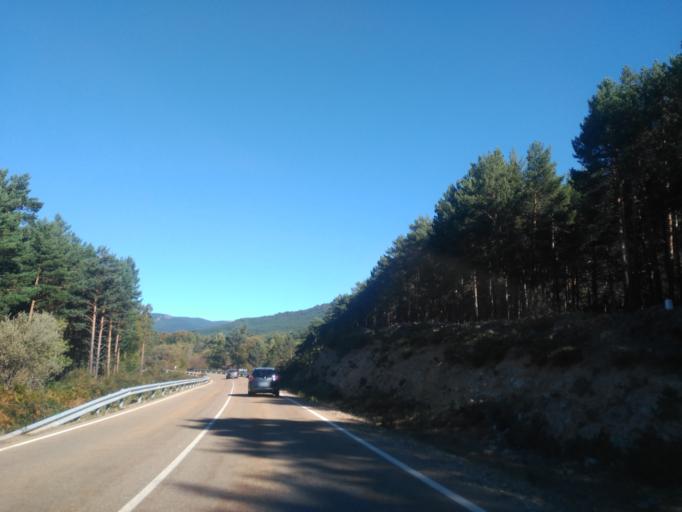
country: ES
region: Castille and Leon
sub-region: Provincia de Soria
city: Vinuesa
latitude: 41.9593
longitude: -2.7767
